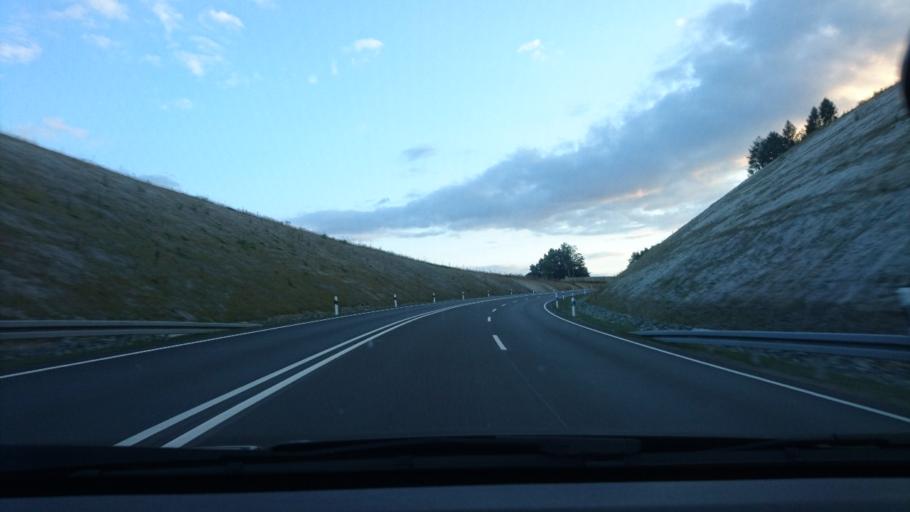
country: DE
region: Saxony
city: Rodewisch
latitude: 50.5323
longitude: 12.3921
